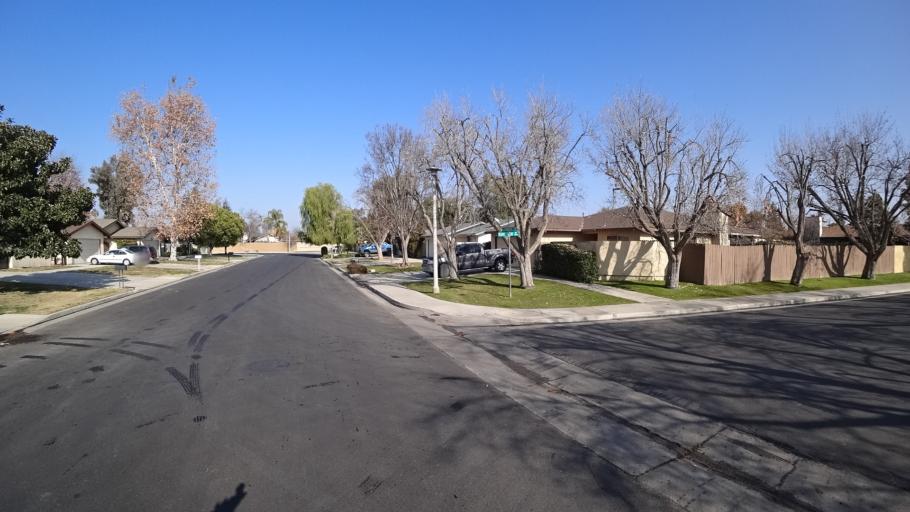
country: US
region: California
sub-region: Kern County
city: Bakersfield
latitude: 35.3248
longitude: -119.0680
